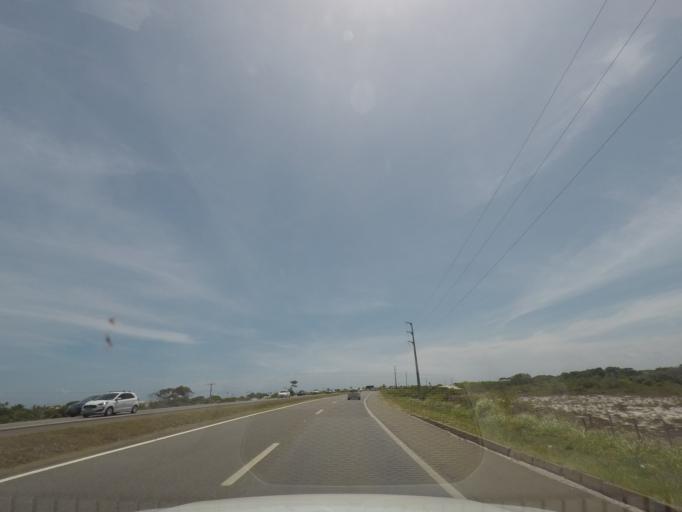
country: BR
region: Bahia
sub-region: Camacari
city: Camacari
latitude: -12.6792
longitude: -38.1047
